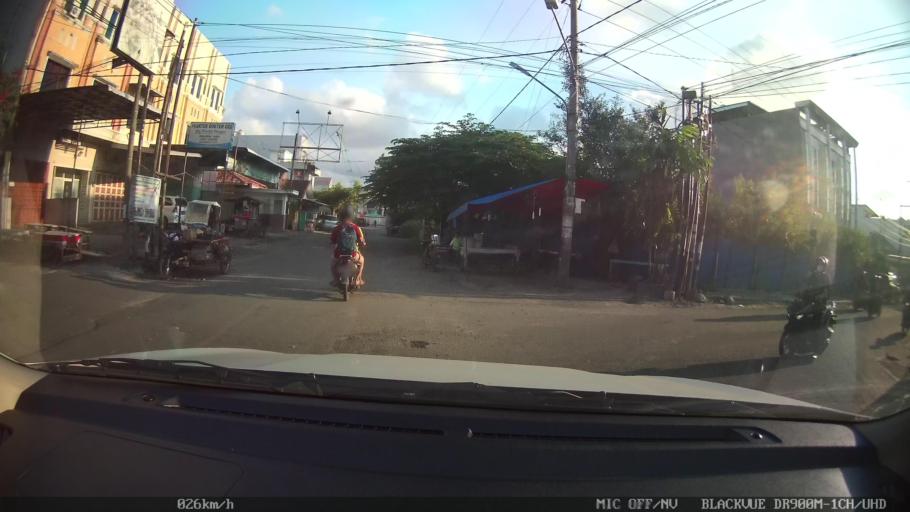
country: ID
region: North Sumatra
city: Medan
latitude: 3.6026
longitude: 98.6651
